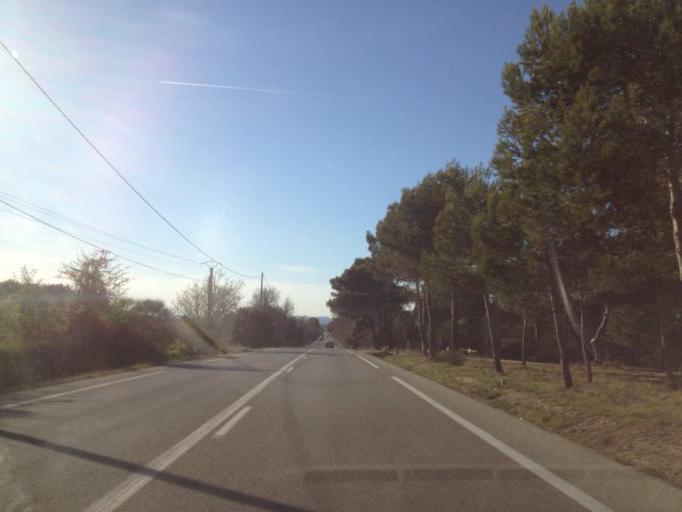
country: FR
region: Provence-Alpes-Cote d'Azur
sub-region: Departement des Bouches-du-Rhone
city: Eguilles
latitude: 43.6041
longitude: 5.3395
